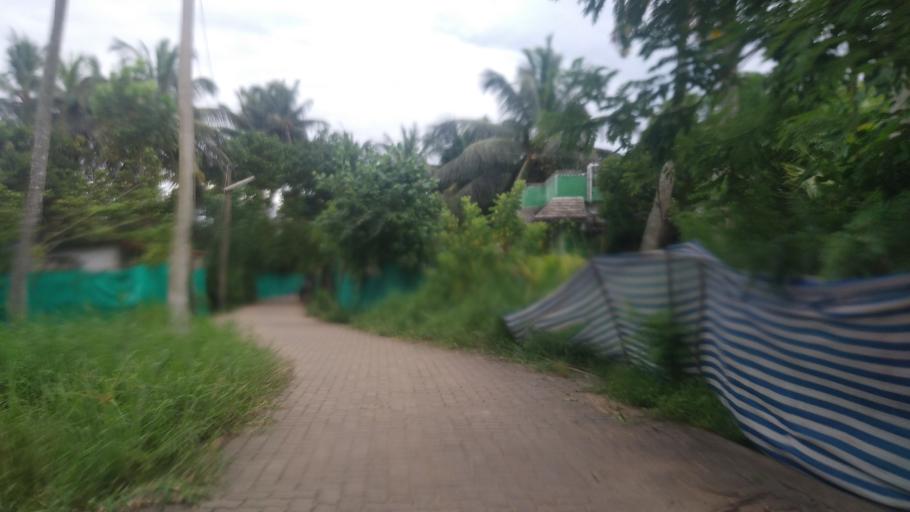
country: IN
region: Kerala
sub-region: Ernakulam
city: Cochin
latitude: 9.8698
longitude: 76.2759
